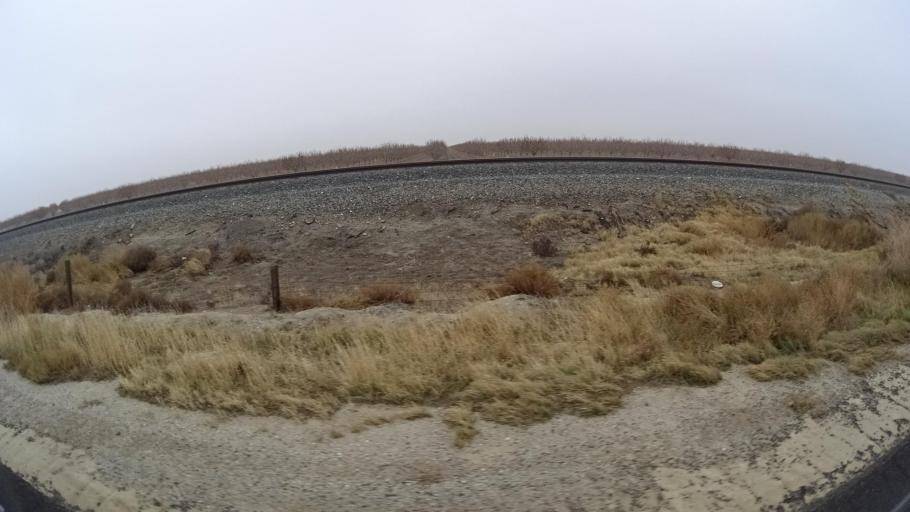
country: US
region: California
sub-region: Kern County
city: Greenfield
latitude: 35.1801
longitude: -119.1834
